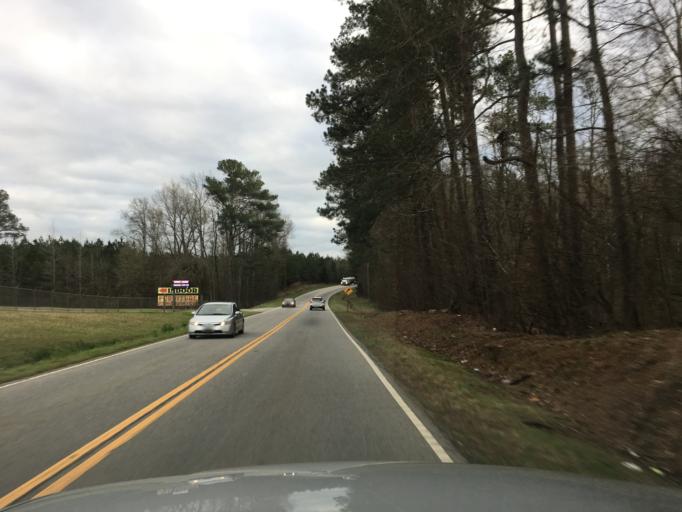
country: US
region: South Carolina
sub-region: Saluda County
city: Saluda
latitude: 33.9860
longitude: -81.7699
